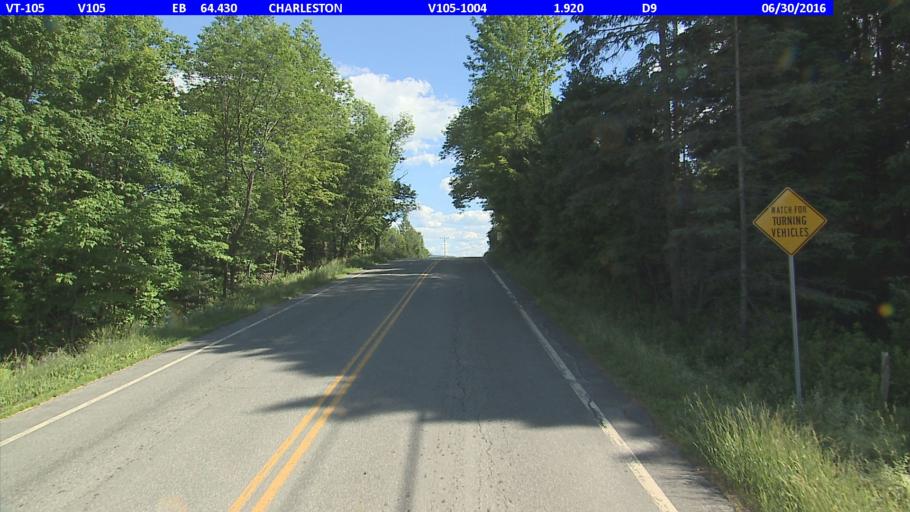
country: US
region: Vermont
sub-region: Orleans County
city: Newport
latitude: 44.8874
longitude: -72.0567
